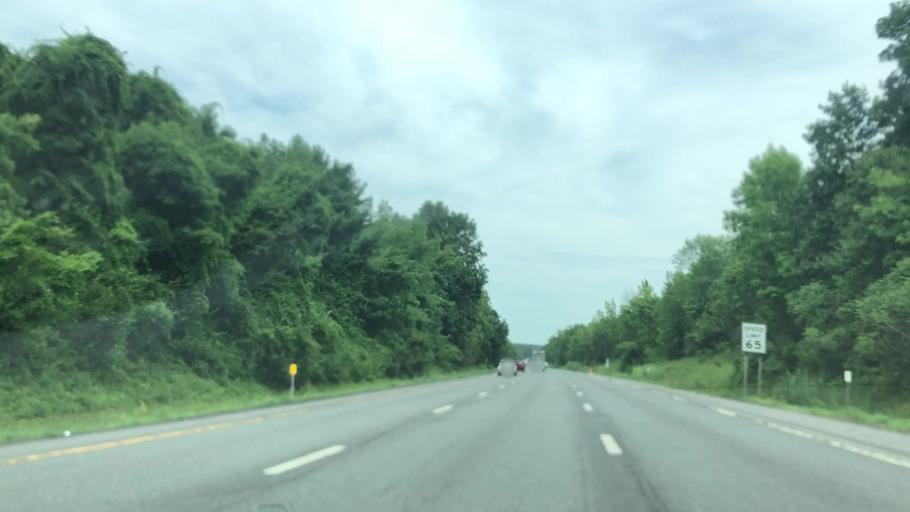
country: US
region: New York
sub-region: Saratoga County
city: Saratoga Springs
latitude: 43.0310
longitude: -73.7816
